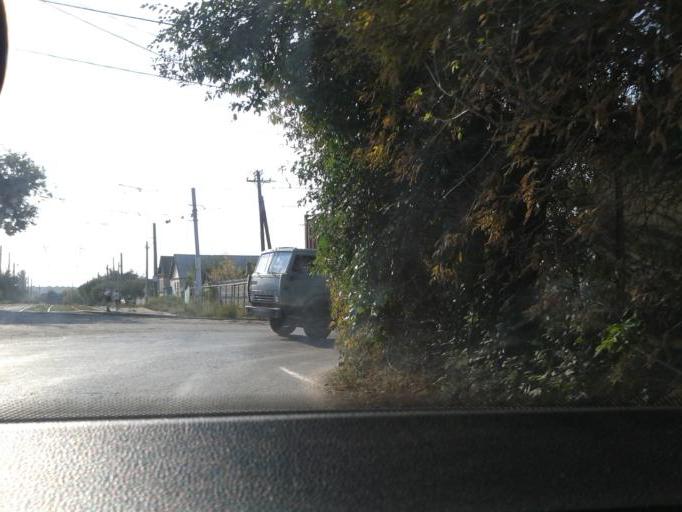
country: RU
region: Volgograd
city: Volgograd
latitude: 48.6927
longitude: 44.4550
